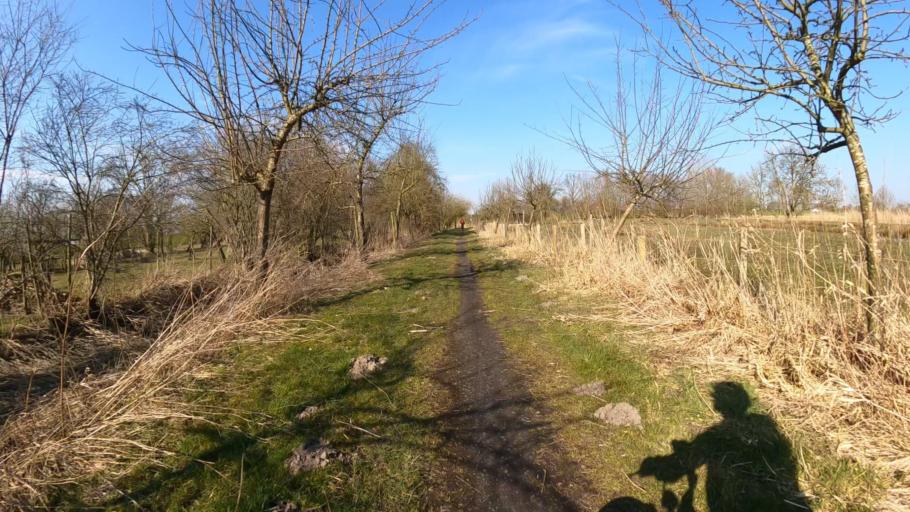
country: DE
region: Schleswig-Holstein
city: Seester
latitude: 53.7200
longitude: 9.5784
